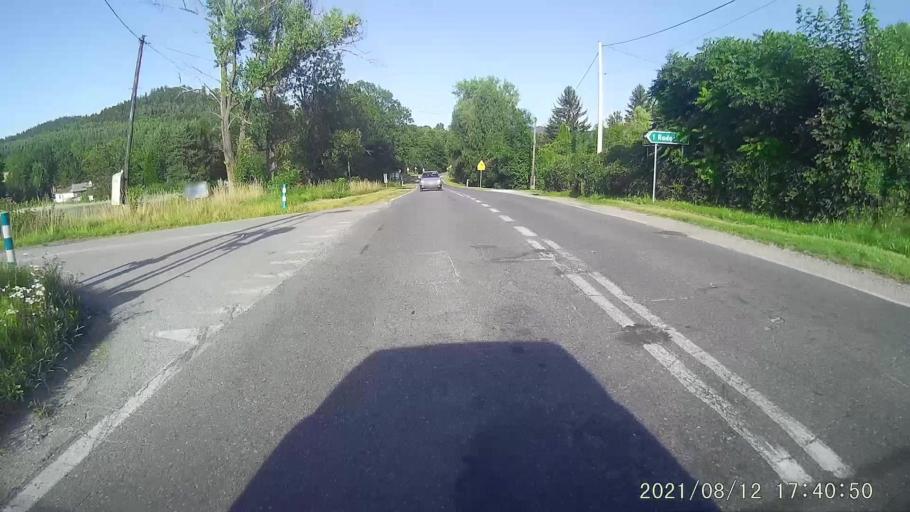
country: PL
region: Lower Silesian Voivodeship
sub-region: Powiat klodzki
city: Ladek-Zdroj
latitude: 50.3408
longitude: 16.8325
